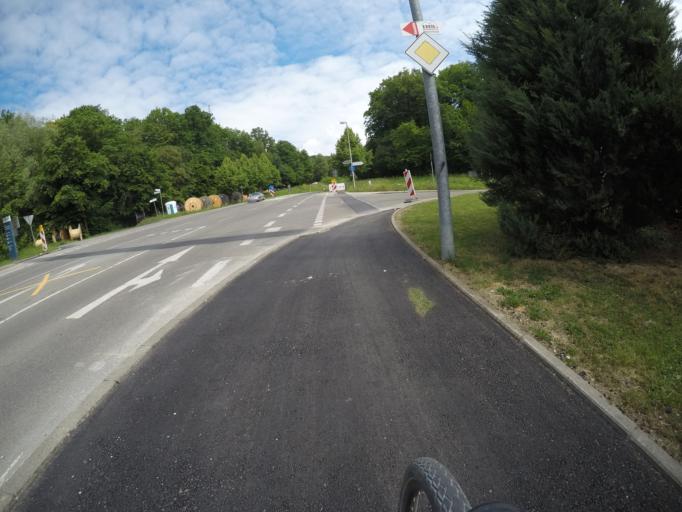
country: DE
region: Baden-Wuerttemberg
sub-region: Regierungsbezirk Stuttgart
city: Notzingen
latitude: 48.6604
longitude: 9.4576
